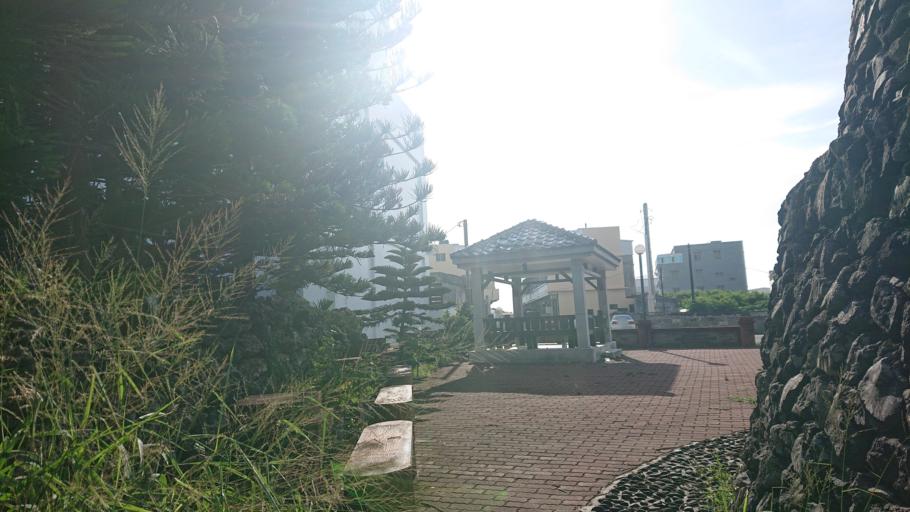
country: TW
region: Taiwan
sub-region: Penghu
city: Ma-kung
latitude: 23.5254
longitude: 119.6026
